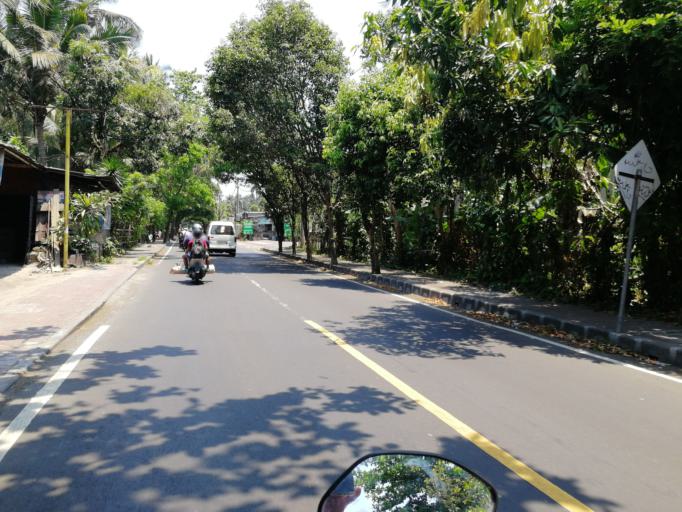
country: ID
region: Bali
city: Banjar Pegeringsingan
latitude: -8.4997
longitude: 115.5557
